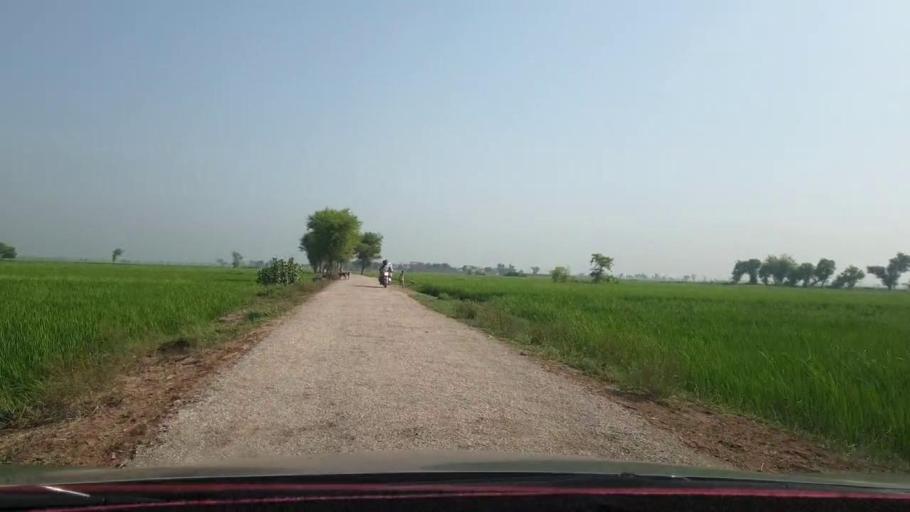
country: PK
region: Sindh
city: Nasirabad
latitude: 27.4698
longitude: 67.9224
